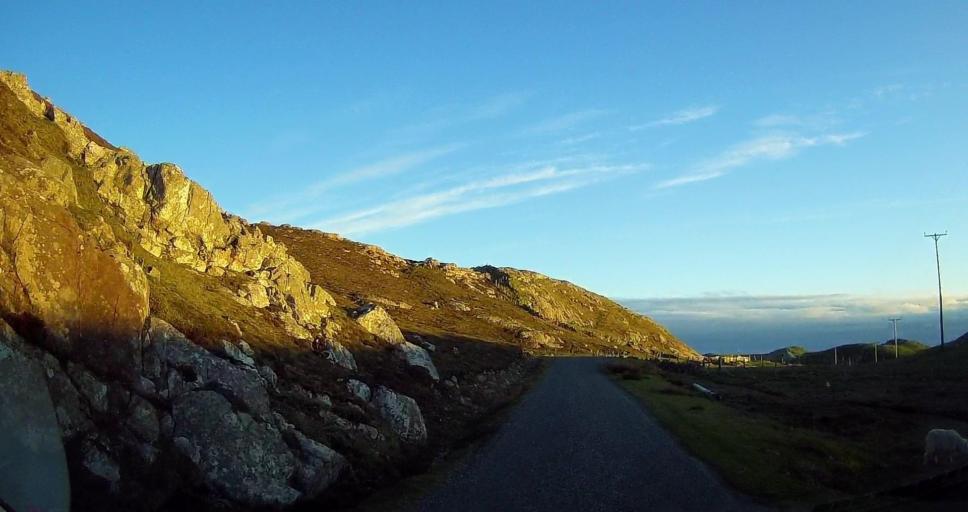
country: GB
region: Scotland
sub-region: Shetland Islands
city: Lerwick
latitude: 60.4446
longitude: -1.4416
